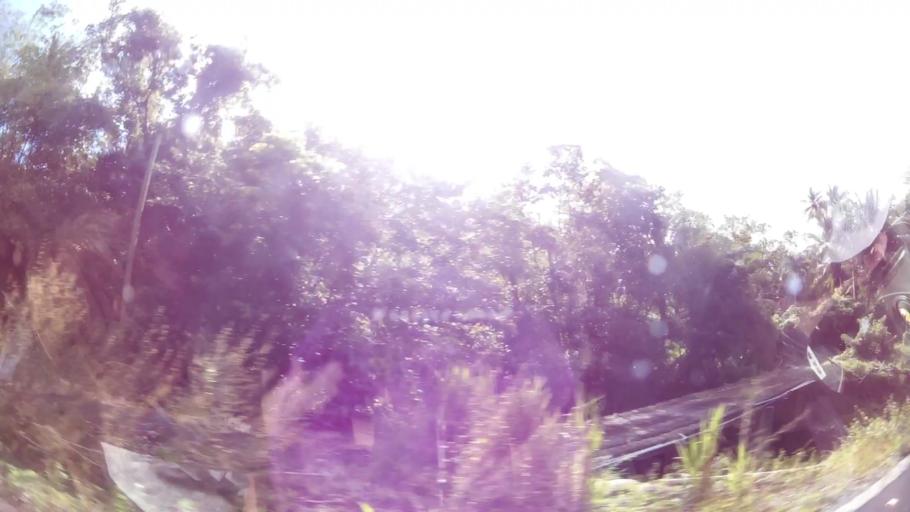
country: DM
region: Saint Andrew
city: Marigot
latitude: 15.5171
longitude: -61.2766
